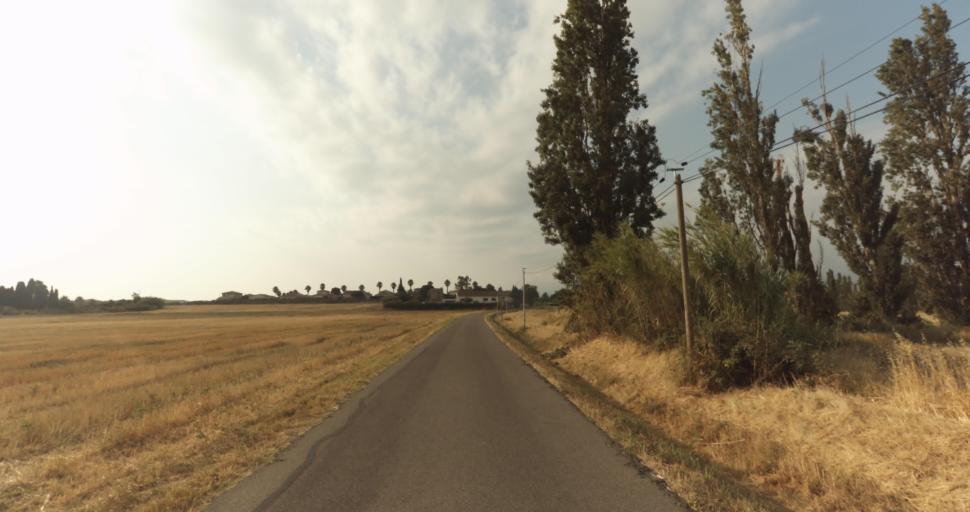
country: FR
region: Languedoc-Roussillon
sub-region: Departement des Pyrenees-Orientales
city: Corneilla-del-Vercol
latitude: 42.6306
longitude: 2.9493
